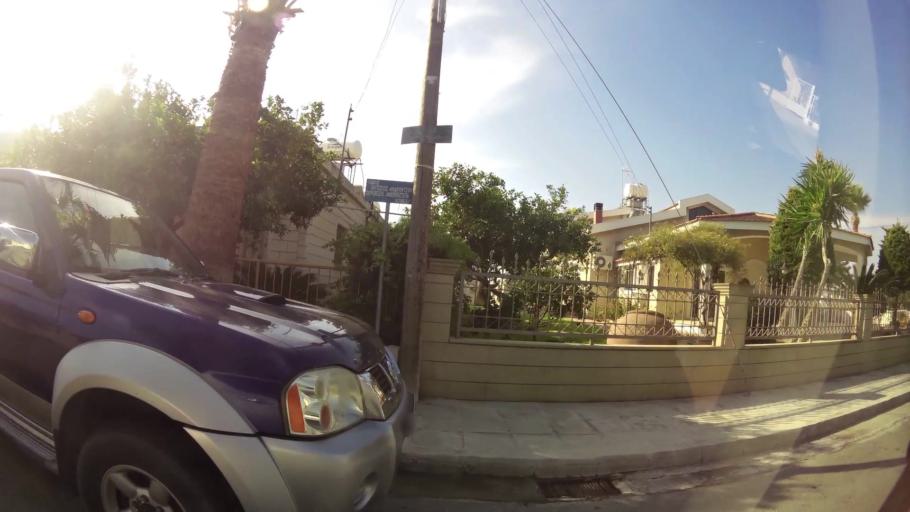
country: CY
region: Larnaka
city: Aradippou
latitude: 34.9537
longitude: 33.5973
